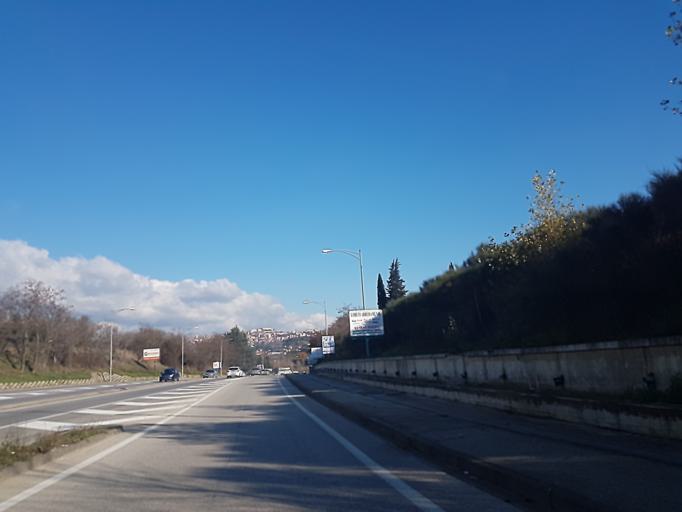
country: IT
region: Umbria
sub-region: Provincia di Perugia
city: Lacugnano
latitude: 43.0819
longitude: 12.3538
